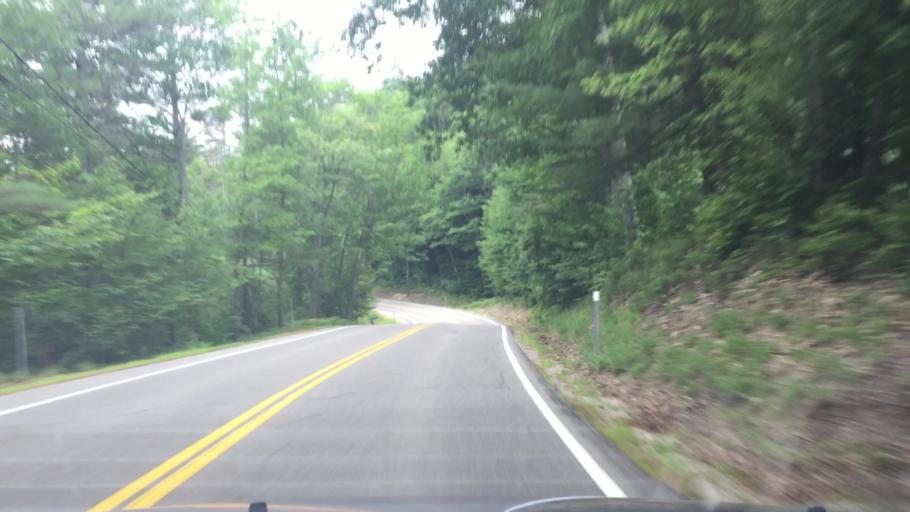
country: US
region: New Hampshire
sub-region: Carroll County
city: Madison
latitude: 43.8941
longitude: -71.0706
